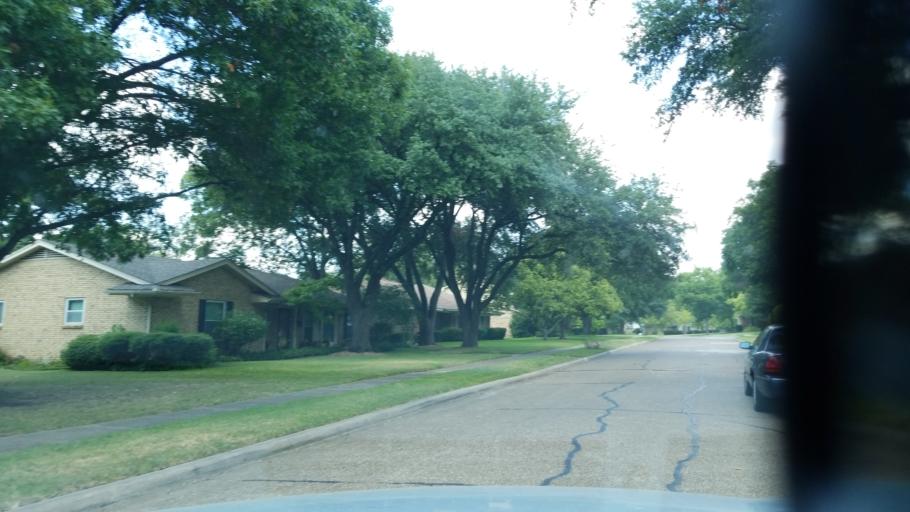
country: US
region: Texas
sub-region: Dallas County
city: Richardson
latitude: 32.9629
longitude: -96.7666
